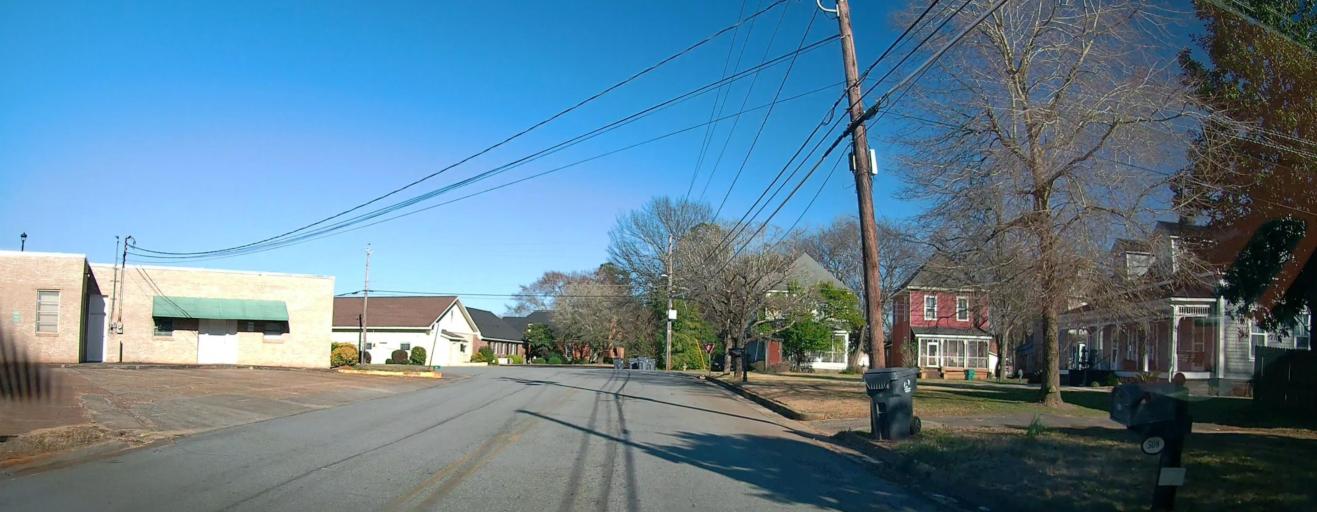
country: US
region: Georgia
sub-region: Sumter County
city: Americus
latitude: 32.0714
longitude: -84.2385
